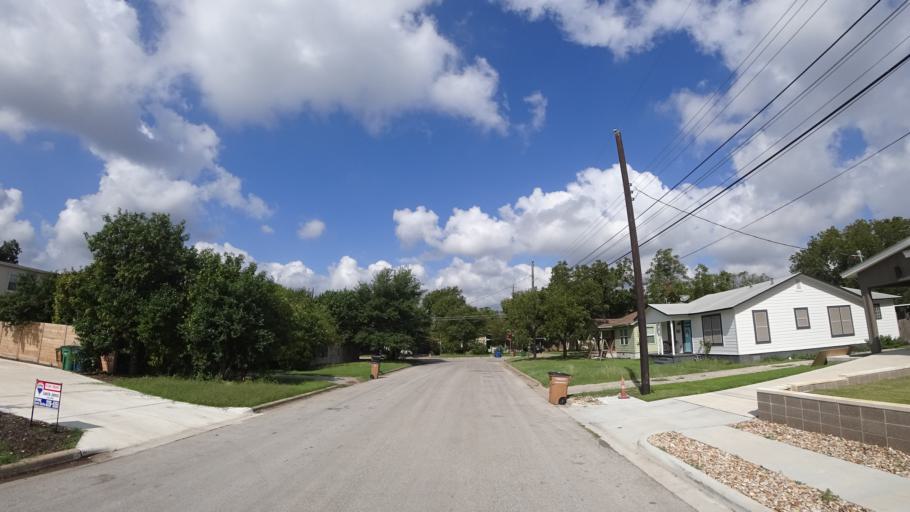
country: US
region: Texas
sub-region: Travis County
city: Austin
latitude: 30.3489
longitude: -97.7188
